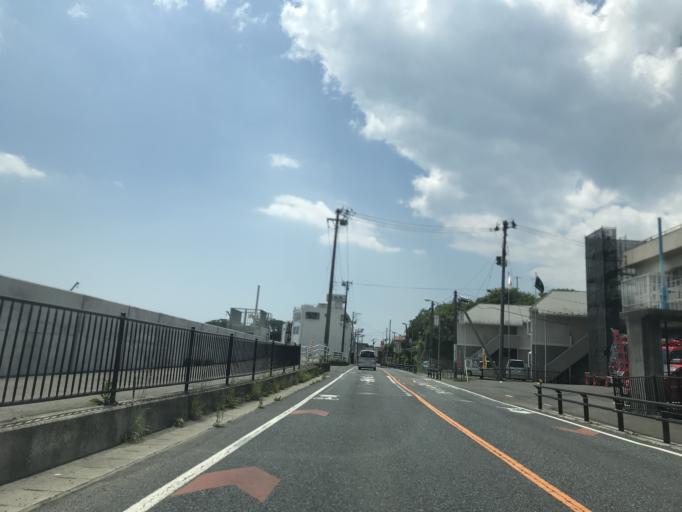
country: JP
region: Miyagi
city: Matsushima
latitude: 38.3785
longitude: 141.0682
